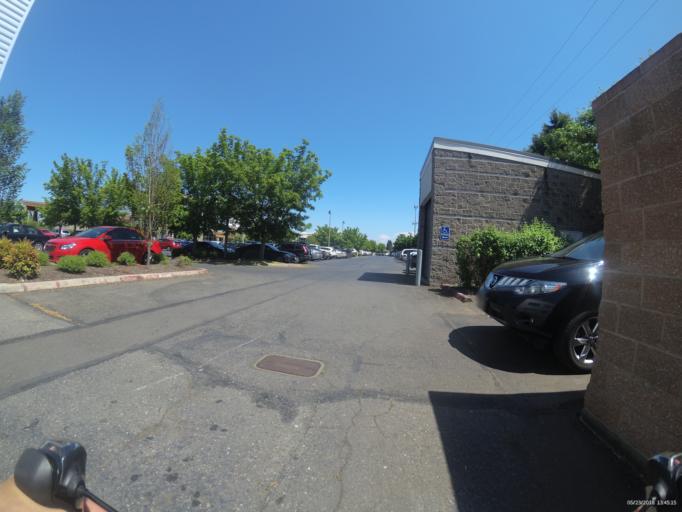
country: US
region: Washington
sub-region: Pierce County
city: Lakewood
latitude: 47.1608
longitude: -122.5181
